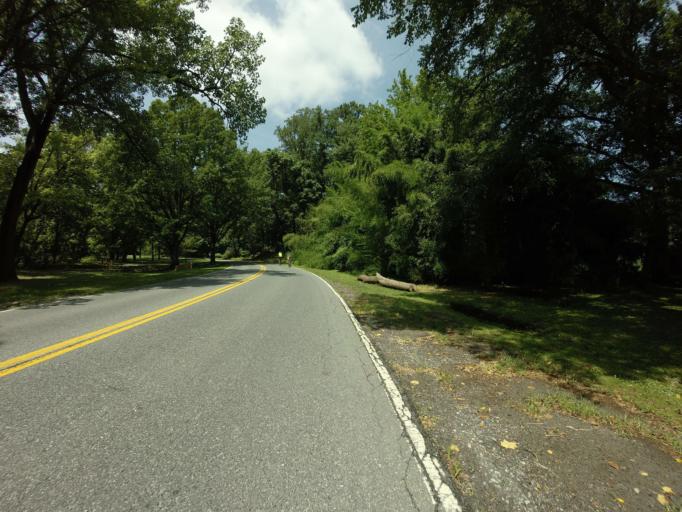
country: US
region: Maryland
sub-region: Montgomery County
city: South Kensington
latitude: 39.0087
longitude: -77.0826
